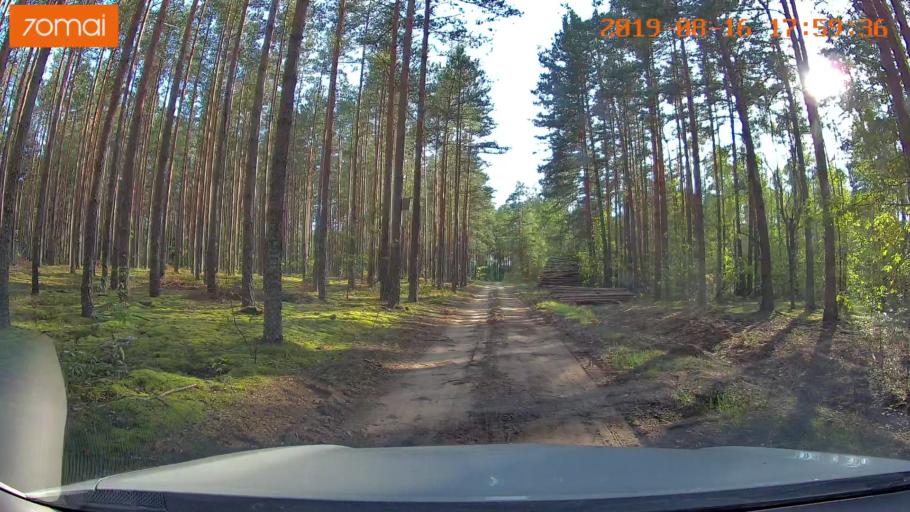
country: BY
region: Mogilev
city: Asipovichy
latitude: 53.2224
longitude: 28.6577
